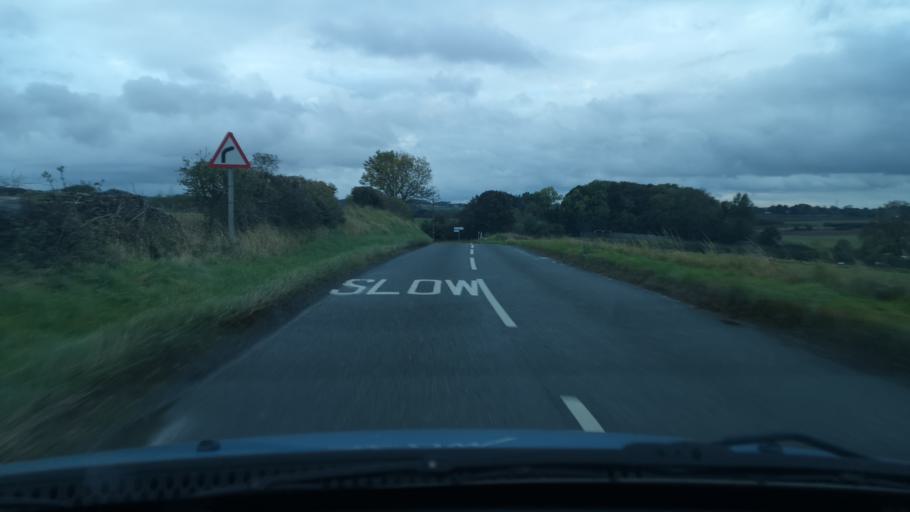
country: GB
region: England
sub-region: Doncaster
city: Norton
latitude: 53.6330
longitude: -1.1999
